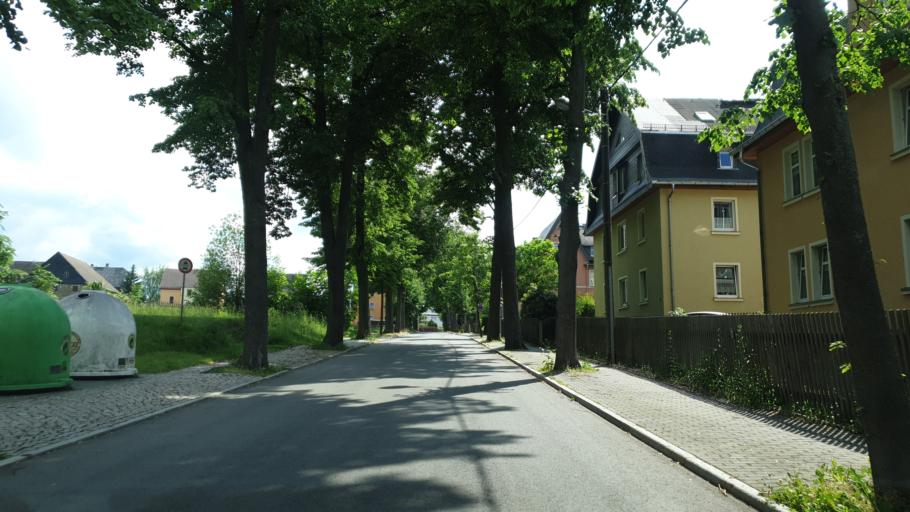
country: DE
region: Saxony
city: Lugau
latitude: 50.7349
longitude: 12.7397
